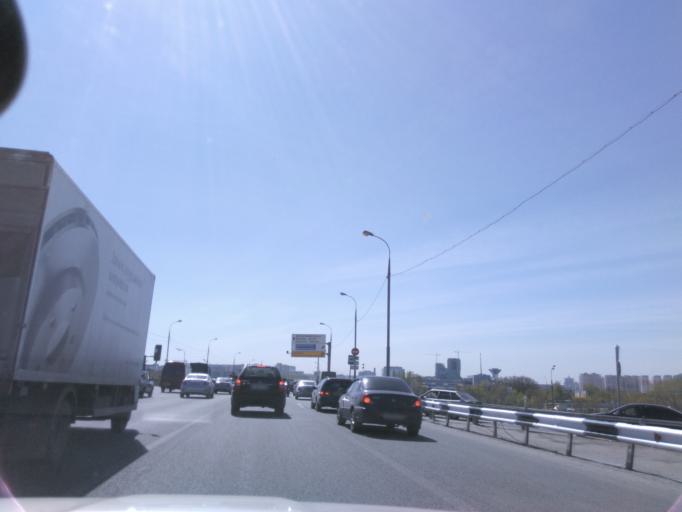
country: RU
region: Moscow
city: Strogino
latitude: 55.8351
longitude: 37.3956
